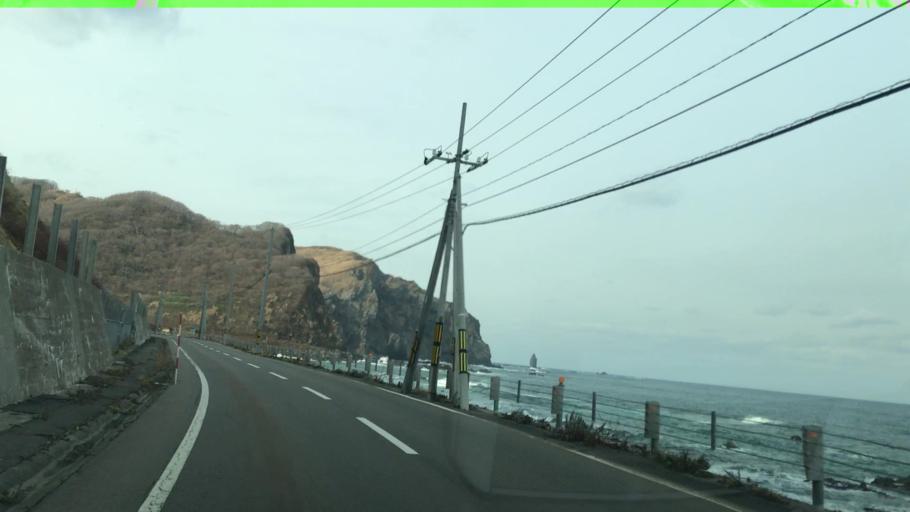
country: JP
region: Hokkaido
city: Iwanai
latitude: 43.3309
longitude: 140.3714
